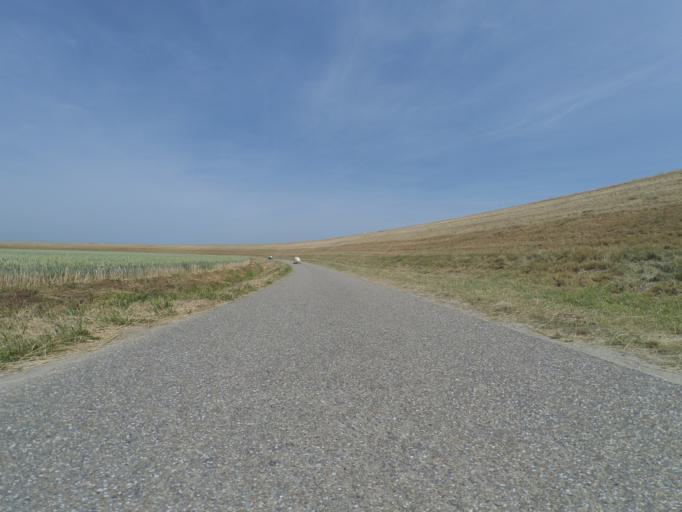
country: NL
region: North Brabant
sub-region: Gemeente Steenbergen
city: Nieuw-Vossemeer
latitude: 51.6374
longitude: 4.1803
